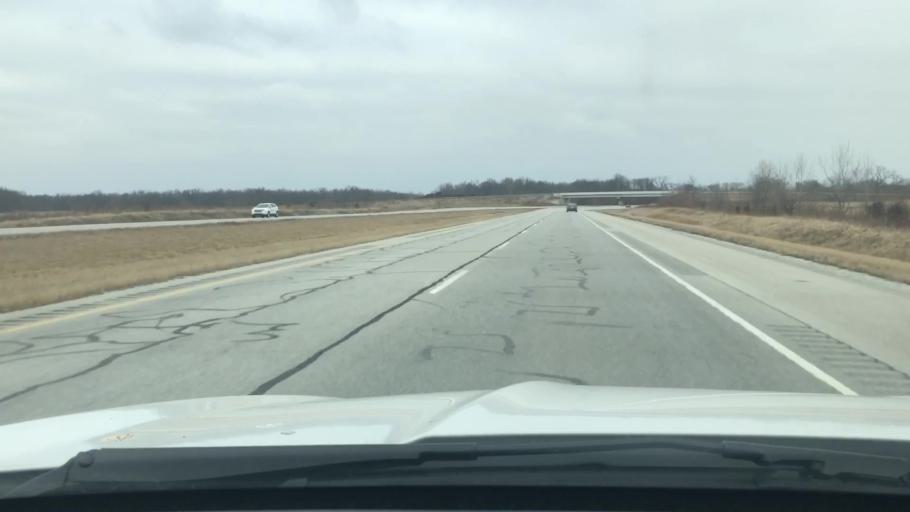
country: US
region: Indiana
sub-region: Carroll County
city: Delphi
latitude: 40.6413
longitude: -86.5810
